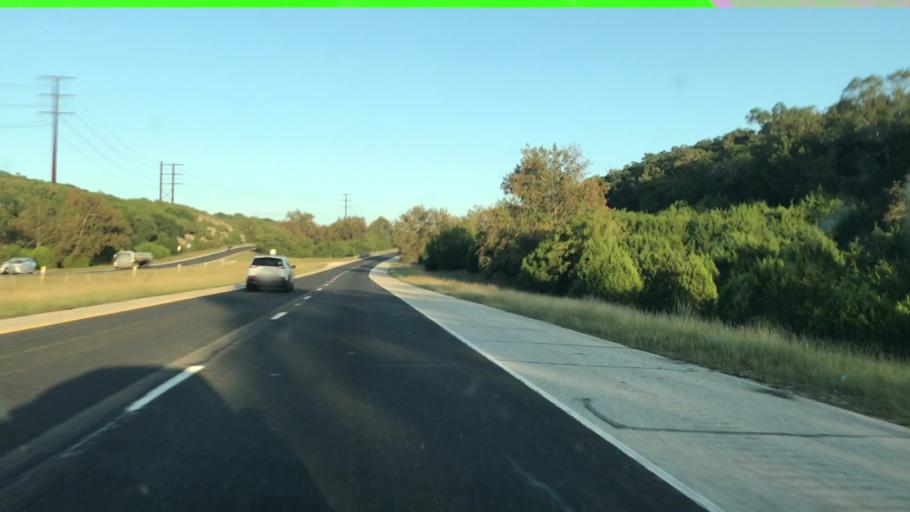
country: US
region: Texas
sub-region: Kerr County
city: Kerrville
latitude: 30.0694
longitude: -99.0866
